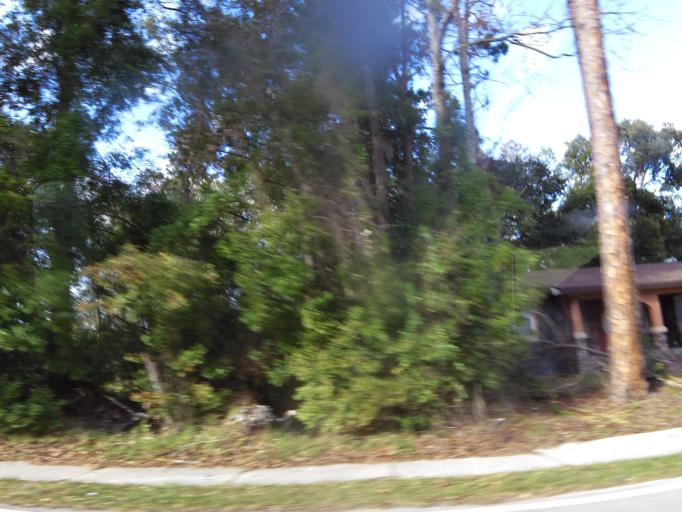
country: US
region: Florida
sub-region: Duval County
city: Jacksonville
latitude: 30.2861
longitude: -81.6122
